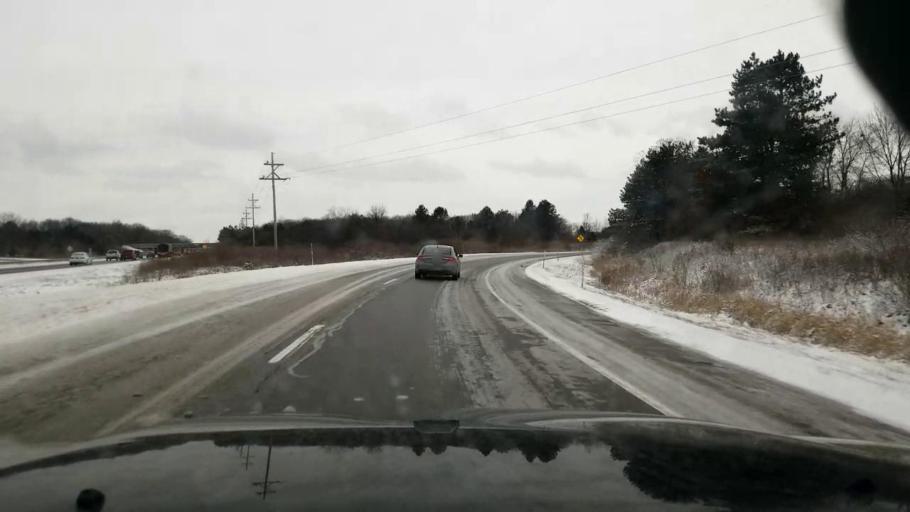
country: US
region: Michigan
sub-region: Jackson County
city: Jackson
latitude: 42.2693
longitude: -84.4714
